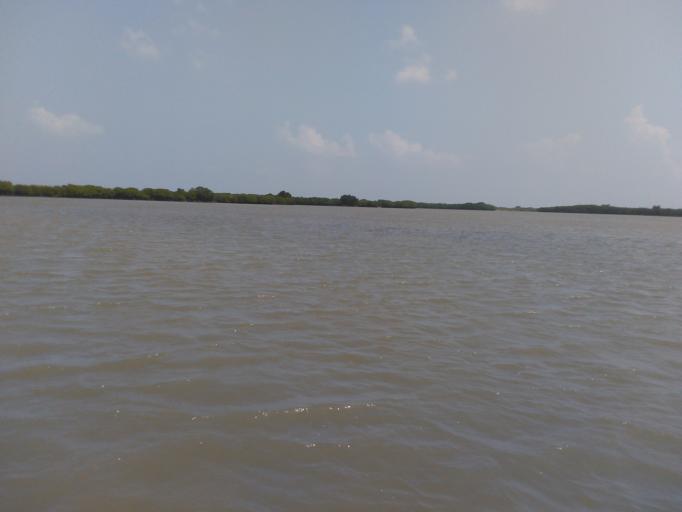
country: IN
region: Tamil Nadu
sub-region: Cuddalore
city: Annamalainagar
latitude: 11.4424
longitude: 79.7914
